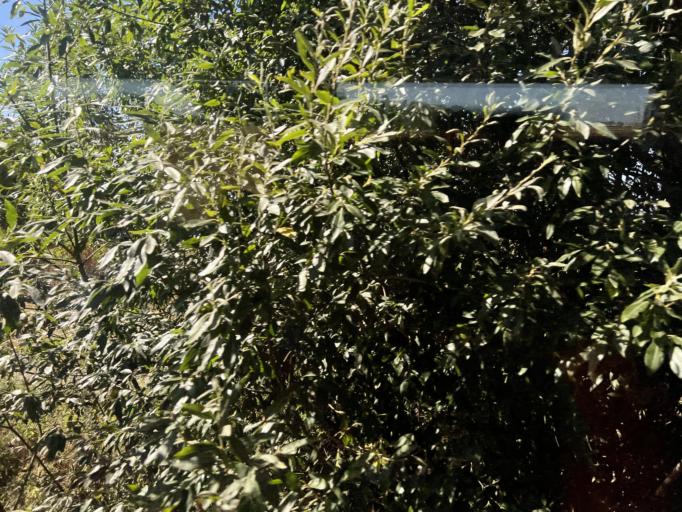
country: GB
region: England
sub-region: Lincolnshire
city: Heckington
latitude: 52.9878
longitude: -0.3490
